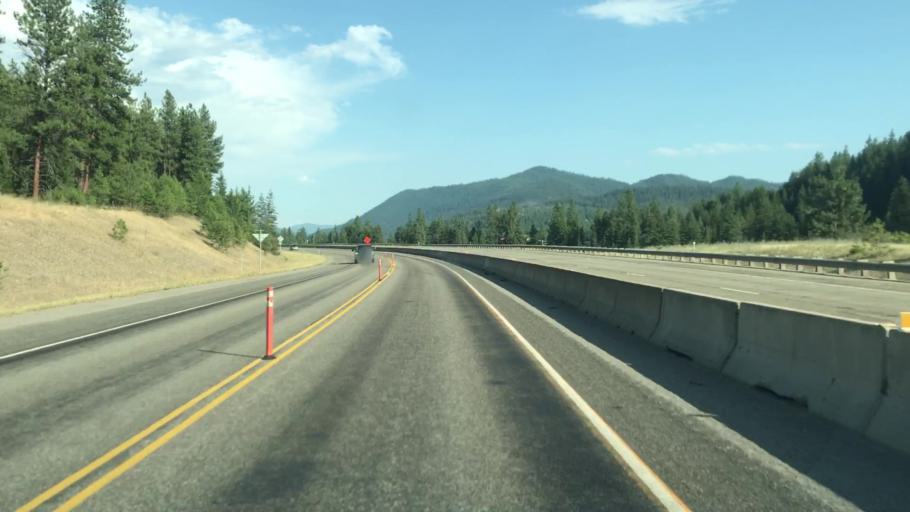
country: US
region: Montana
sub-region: Mineral County
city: Superior
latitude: 47.2190
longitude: -114.9581
